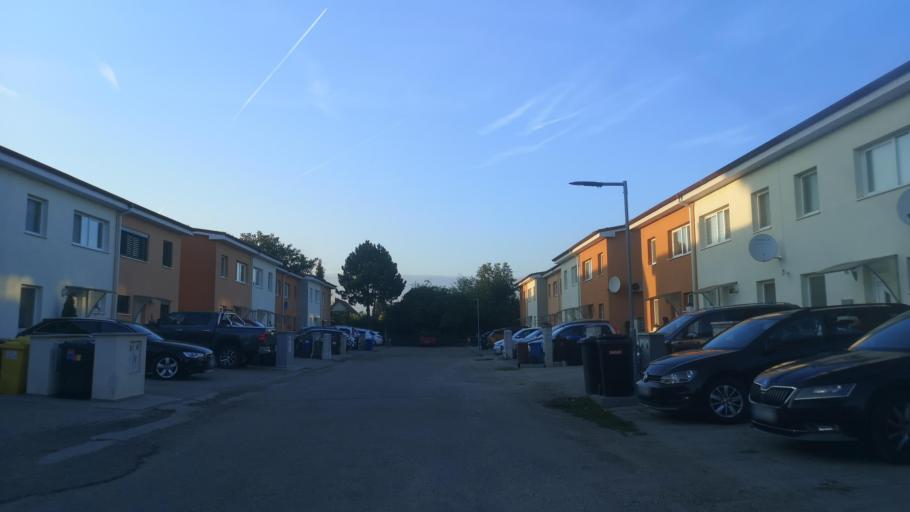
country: SK
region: Nitriansky
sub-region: Okres Nitra
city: Nitra
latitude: 48.2486
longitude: 18.1087
